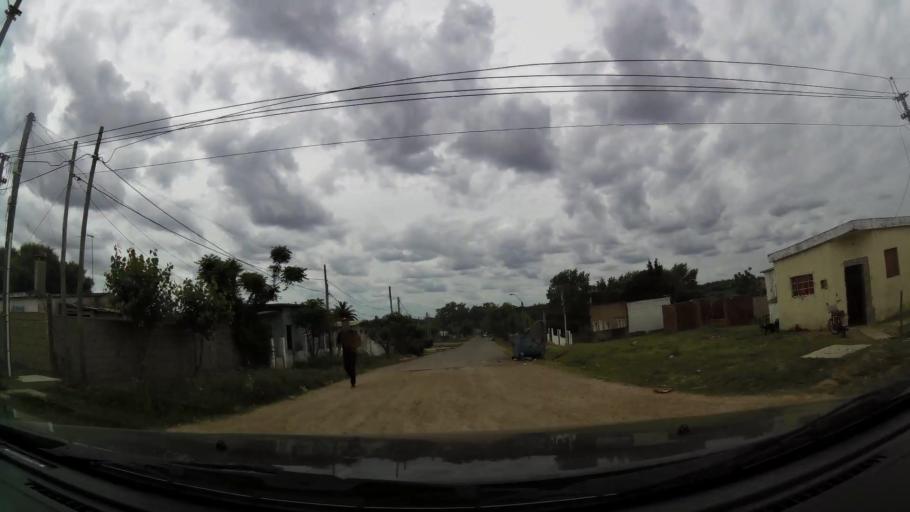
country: UY
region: Canelones
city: Las Piedras
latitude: -34.7150
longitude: -56.2072
